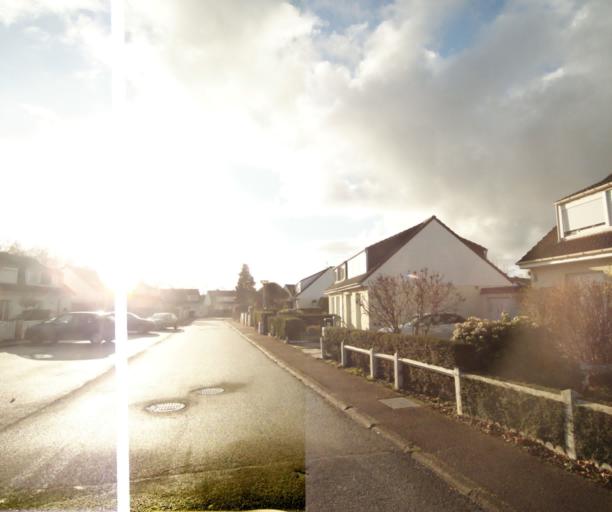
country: FR
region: Ile-de-France
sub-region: Departement des Yvelines
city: Meulan-en-Yvelines
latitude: 49.0103
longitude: 1.9200
